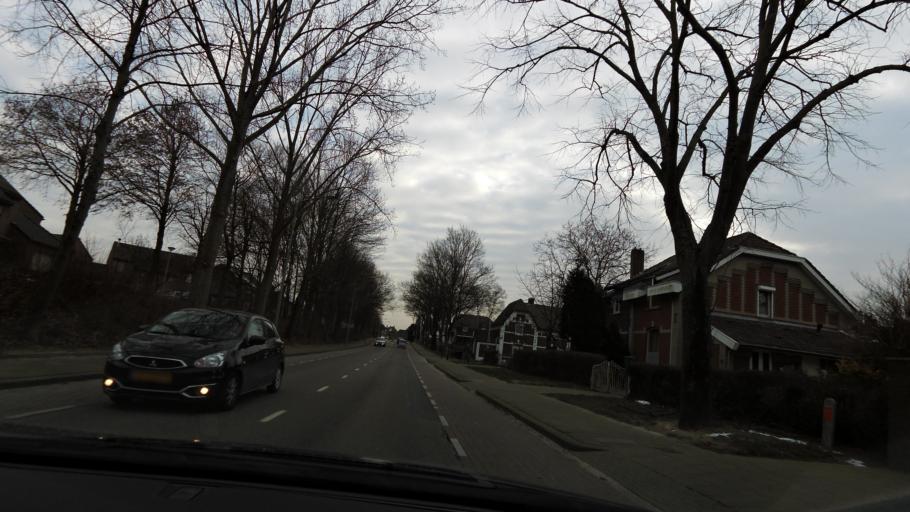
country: NL
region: Limburg
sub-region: Gemeente Heerlen
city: Nieuw-Lotbroek
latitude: 50.9104
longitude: 5.9536
